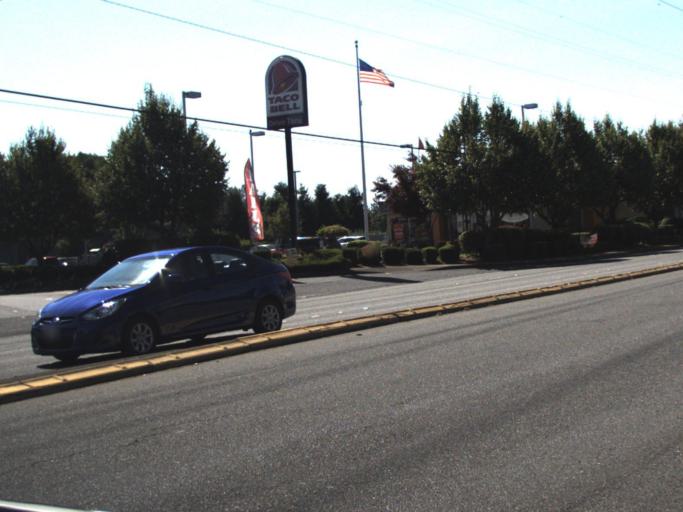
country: US
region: Washington
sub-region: King County
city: Kent
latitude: 47.3795
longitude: -122.2474
